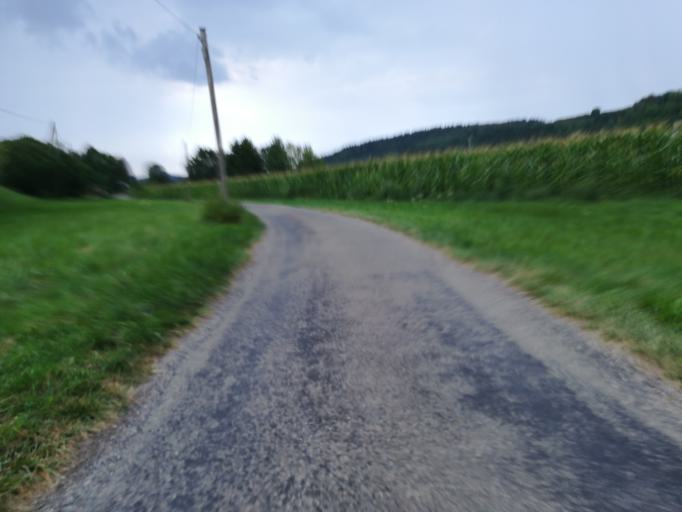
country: DE
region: Baden-Wuerttemberg
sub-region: Freiburg Region
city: Hilzingen
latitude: 47.7574
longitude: 8.8064
